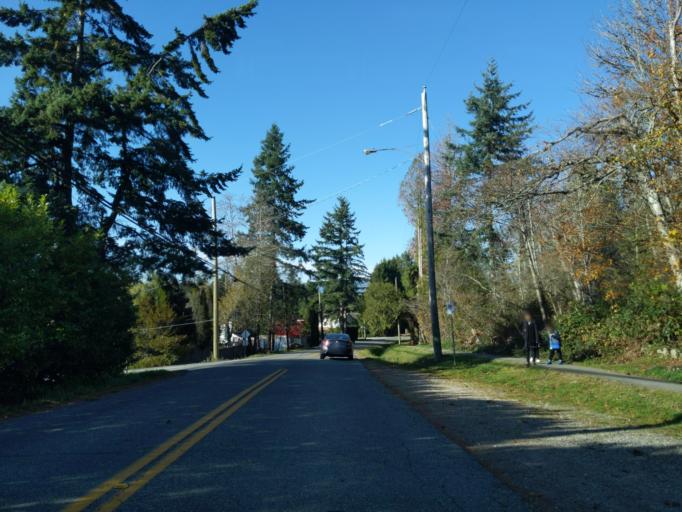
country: CA
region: British Columbia
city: New Westminster
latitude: 49.1934
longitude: -122.8652
